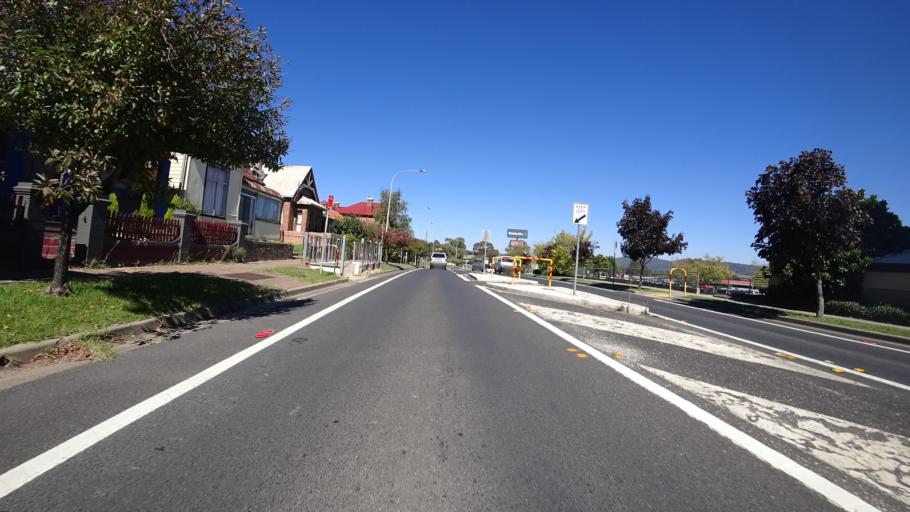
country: AU
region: New South Wales
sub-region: Lithgow
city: Lithgow
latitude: -33.4827
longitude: 150.1560
